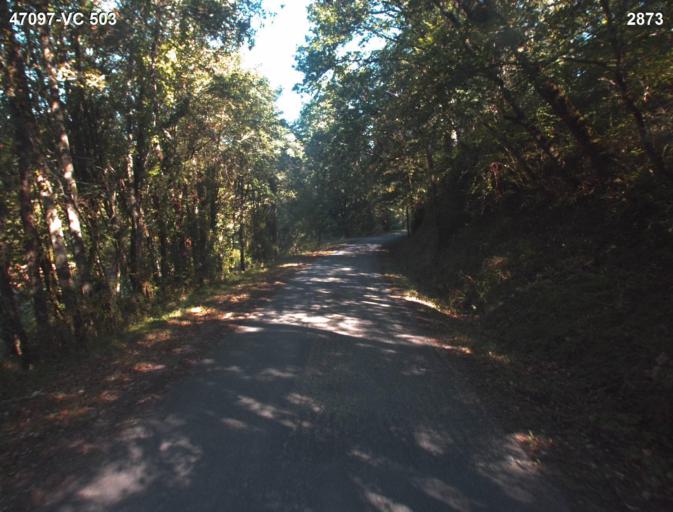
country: FR
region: Aquitaine
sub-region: Departement du Lot-et-Garonne
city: Port-Sainte-Marie
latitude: 44.2146
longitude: 0.3716
